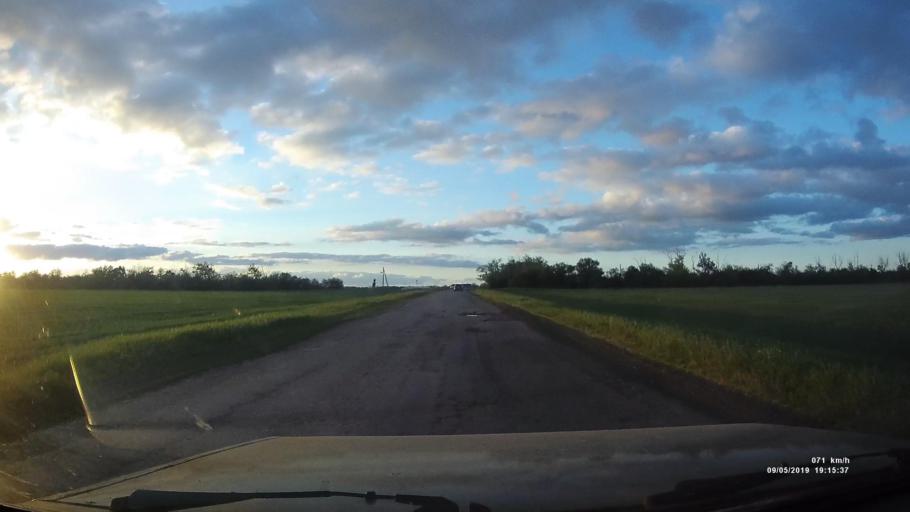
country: RU
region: Krasnodarskiy
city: Kanelovskaya
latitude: 46.7694
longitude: 39.2113
